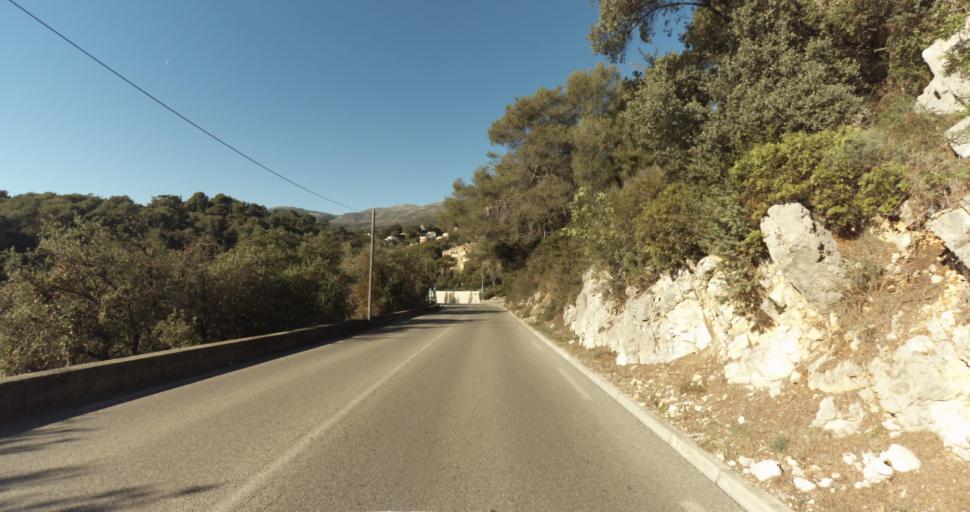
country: FR
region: Provence-Alpes-Cote d'Azur
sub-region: Departement des Alpes-Maritimes
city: Vence
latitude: 43.7144
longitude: 7.1198
